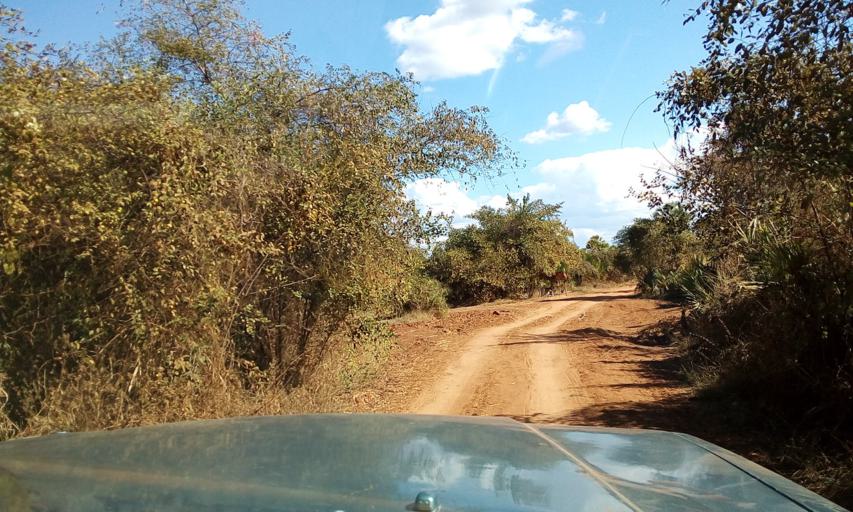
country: MG
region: Boeny
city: Mahajanga
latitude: -16.0551
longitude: 45.8102
